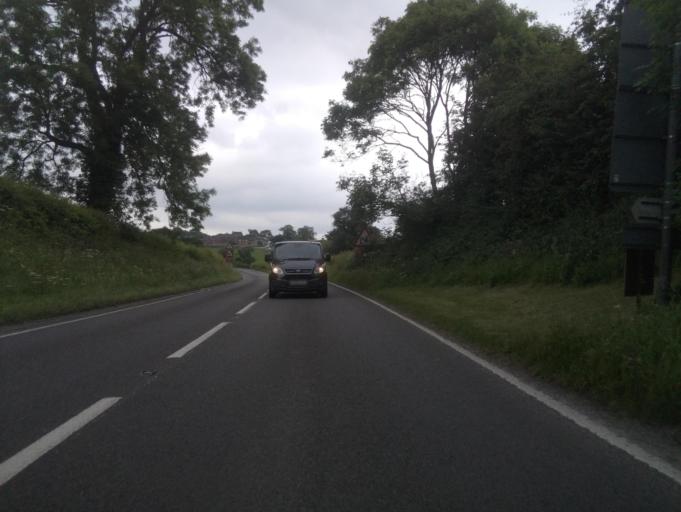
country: GB
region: England
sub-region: Staffordshire
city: Mayfield
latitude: 52.9414
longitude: -1.7613
